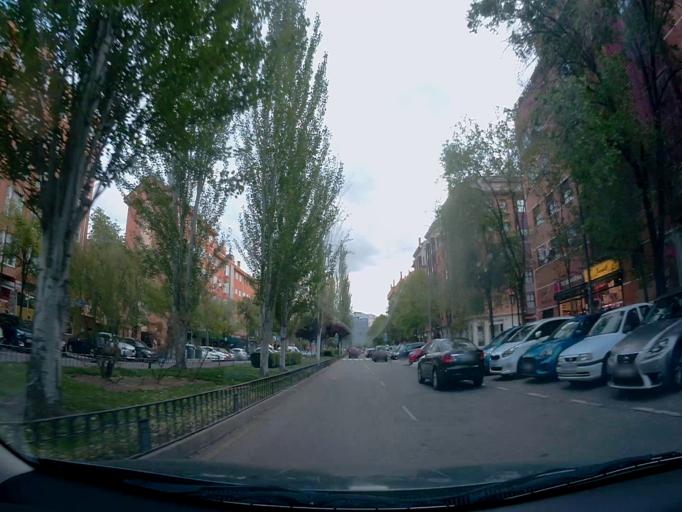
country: ES
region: Madrid
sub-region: Provincia de Madrid
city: Alcorcon
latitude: 40.3468
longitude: -3.8414
